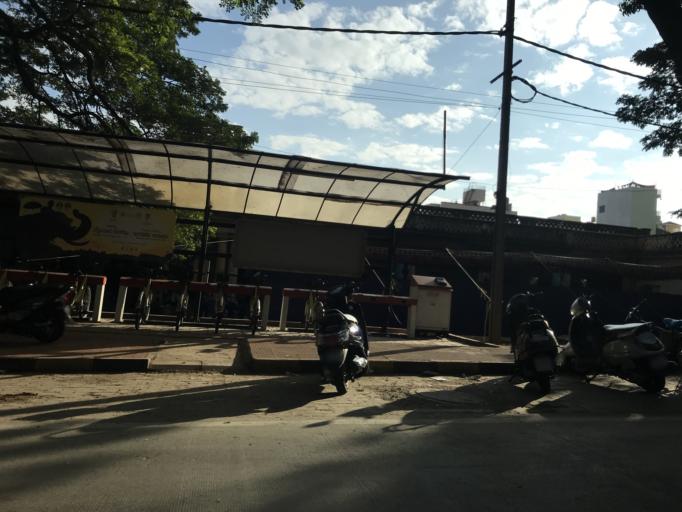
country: IN
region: Karnataka
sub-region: Mysore
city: Mysore
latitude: 12.3022
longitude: 76.6464
